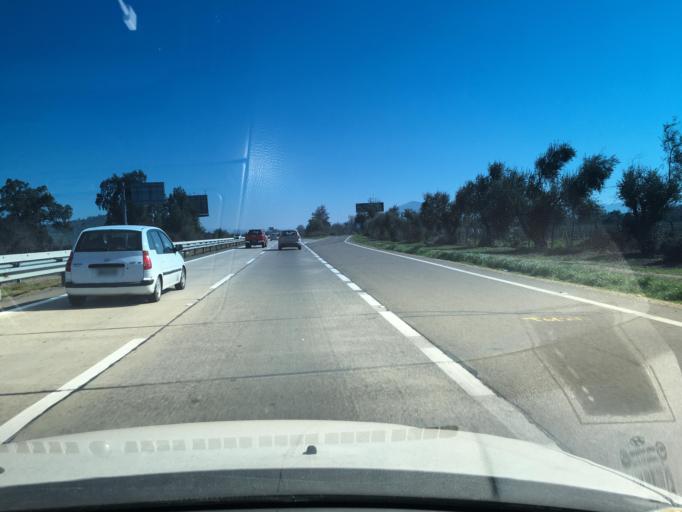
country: CL
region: Valparaiso
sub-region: Provincia de Marga Marga
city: Villa Alemana
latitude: -33.3631
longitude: -71.3162
